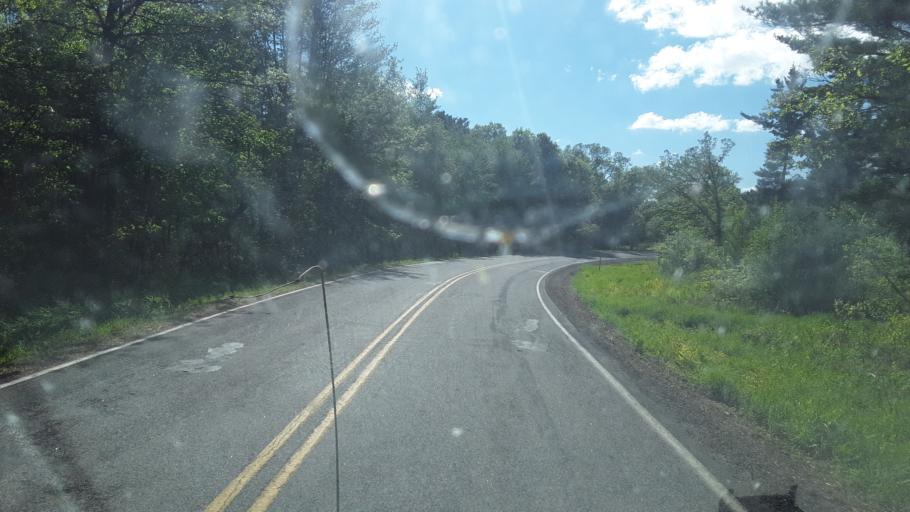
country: US
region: Wisconsin
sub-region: Wood County
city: Nekoosa
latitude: 44.3217
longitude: -90.1283
